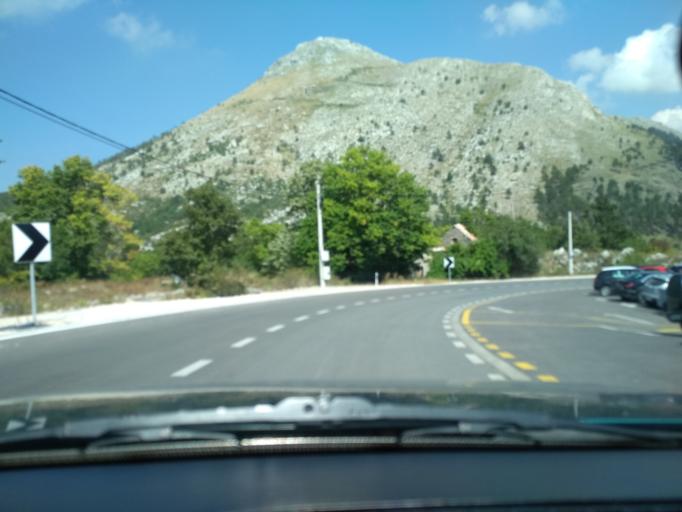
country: ME
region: Kotor
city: Kotor
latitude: 42.4268
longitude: 18.8001
